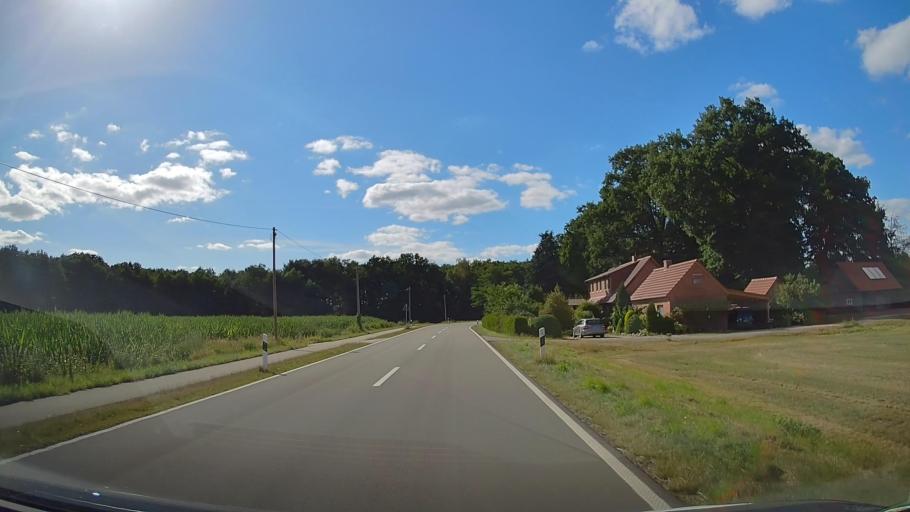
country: DE
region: Lower Saxony
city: Menslage
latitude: 52.6864
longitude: 7.7766
